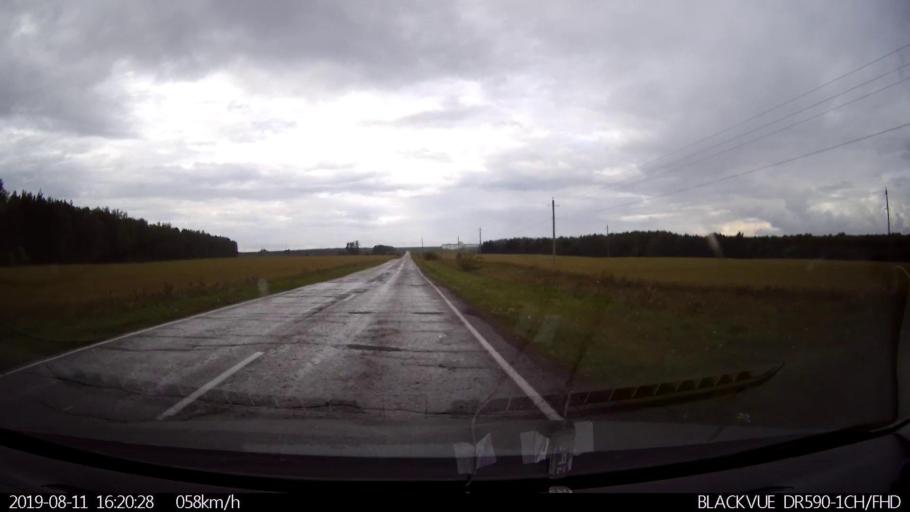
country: RU
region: Ulyanovsk
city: Mayna
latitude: 54.0719
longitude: 47.6028
